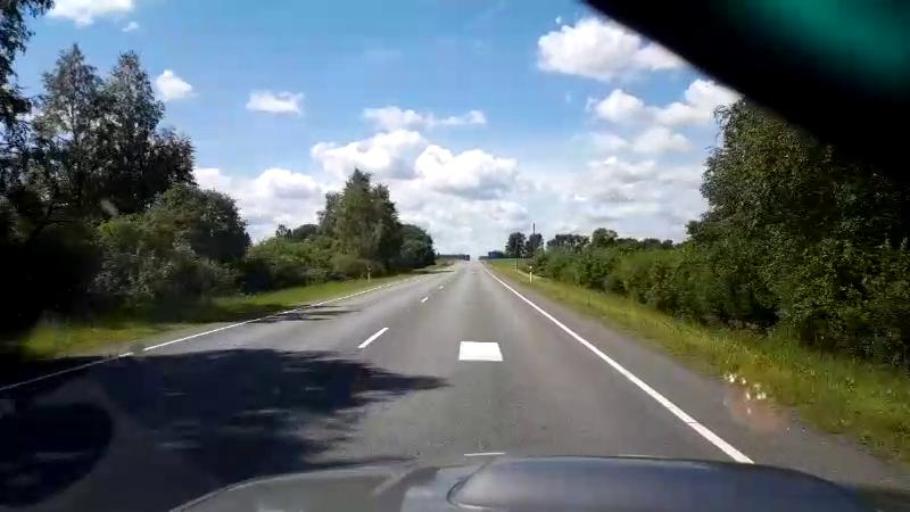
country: EE
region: Laeaene-Virumaa
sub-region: Tapa vald
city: Tapa
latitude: 59.1966
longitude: 25.8306
